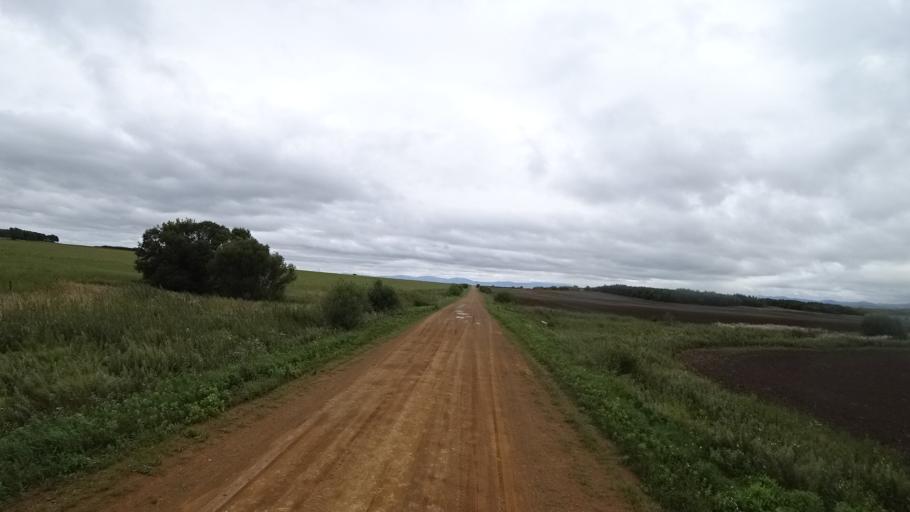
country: RU
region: Primorskiy
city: Chernigovka
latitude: 44.4364
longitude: 132.5849
